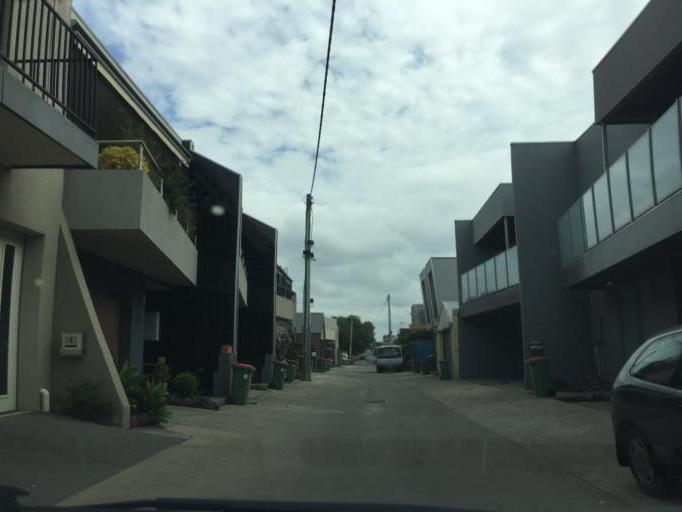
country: AU
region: Victoria
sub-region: Maribyrnong
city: Seddon
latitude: -37.8045
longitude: 144.8907
